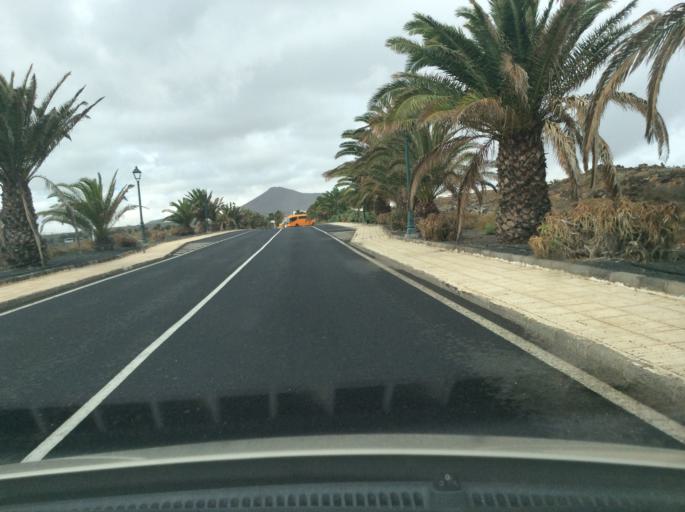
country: ES
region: Canary Islands
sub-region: Provincia de Las Palmas
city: Arrecife
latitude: 28.9829
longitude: -13.5132
